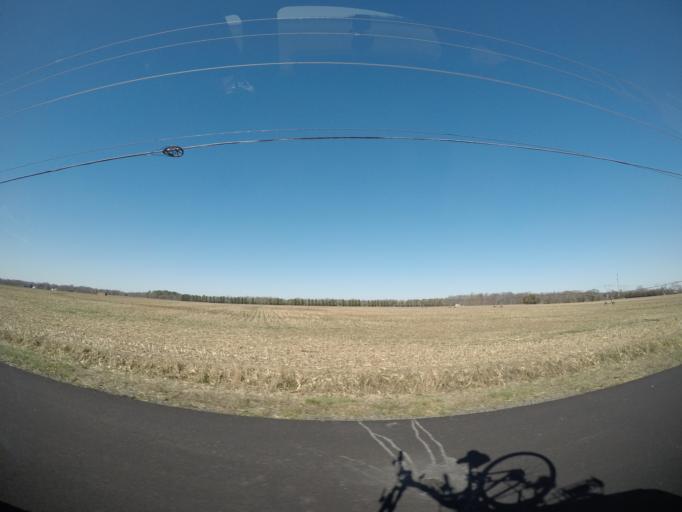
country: US
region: Delaware
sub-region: New Castle County
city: Townsend
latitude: 39.3575
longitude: -75.8327
